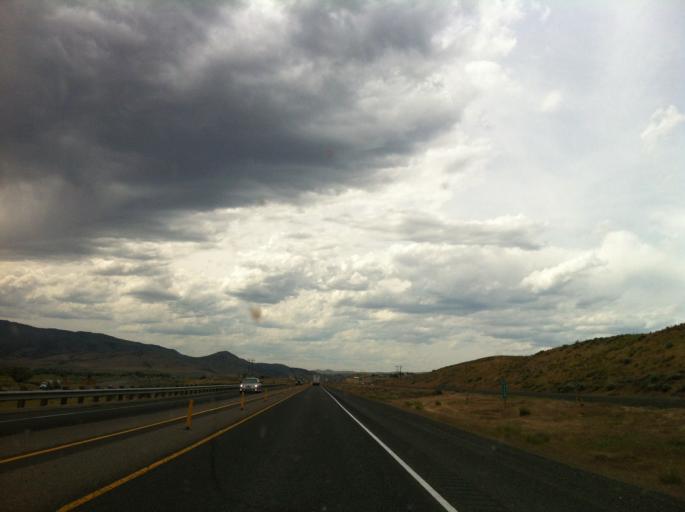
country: US
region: Oregon
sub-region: Baker County
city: Baker City
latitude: 44.5579
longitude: -117.4273
